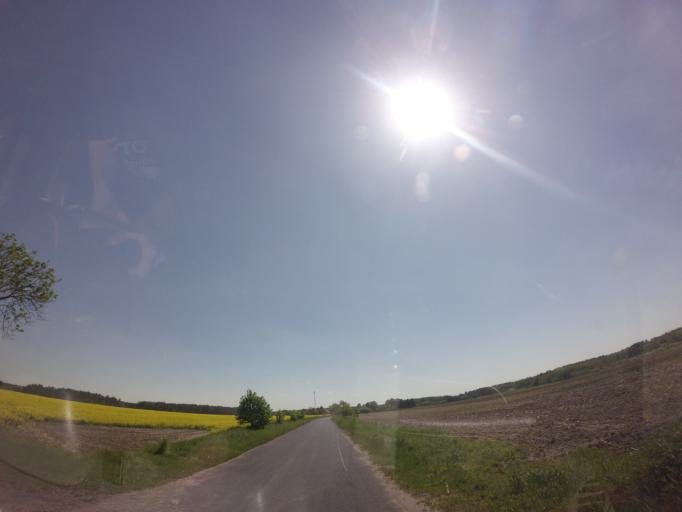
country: PL
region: West Pomeranian Voivodeship
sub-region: Powiat mysliborski
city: Nowogrodek Pomorski
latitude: 52.9429
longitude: 14.9815
